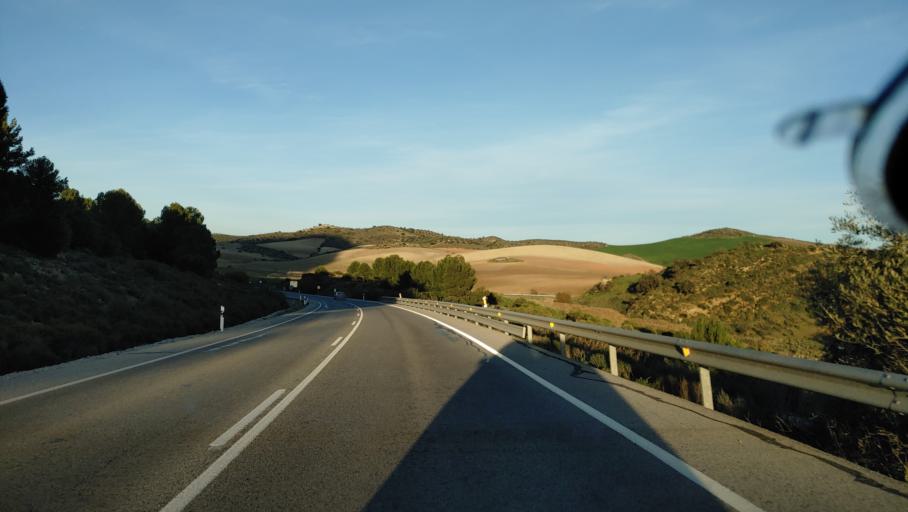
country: ES
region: Andalusia
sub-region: Provincia de Malaga
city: Campillos
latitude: 36.9732
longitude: -4.8362
